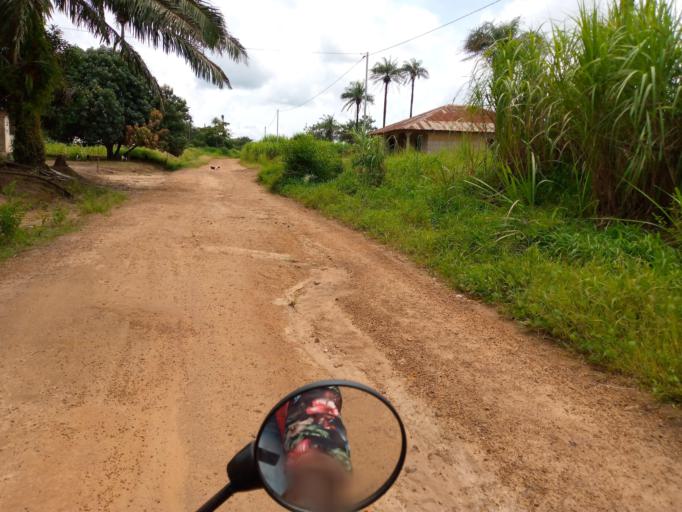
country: SL
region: Northern Province
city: Binkolo
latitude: 9.1114
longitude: -12.1969
